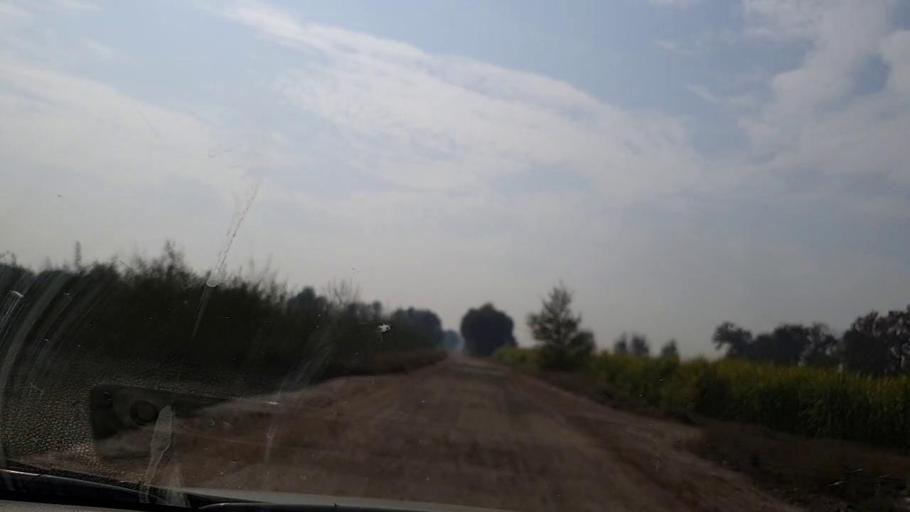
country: PK
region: Sindh
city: Daulatpur
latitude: 26.5272
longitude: 67.9794
